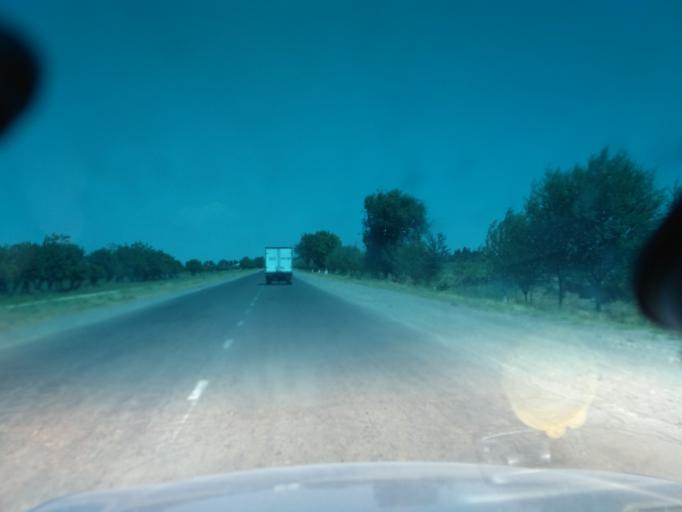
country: UZ
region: Sirdaryo
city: Guliston
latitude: 40.4870
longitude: 68.8899
